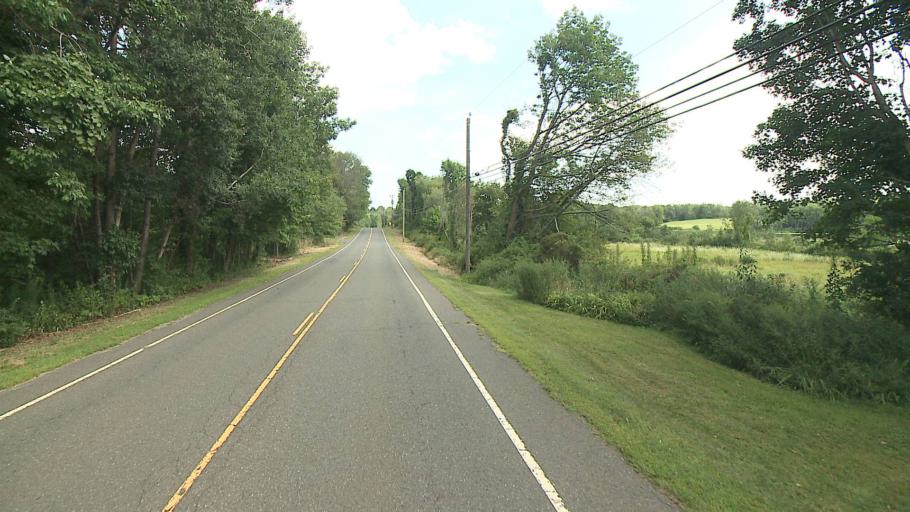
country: US
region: Connecticut
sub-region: Litchfield County
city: Bethlehem Village
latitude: 41.6494
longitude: -73.1900
